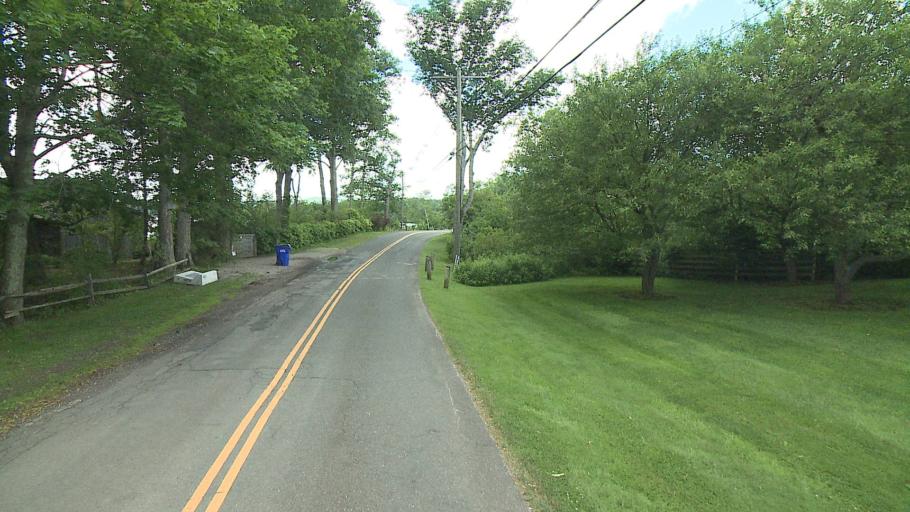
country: US
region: Connecticut
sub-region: Litchfield County
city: New Preston
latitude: 41.7010
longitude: -73.3648
